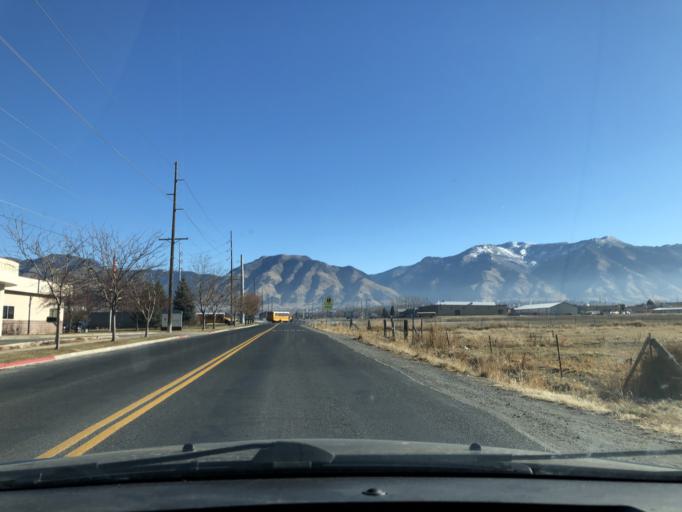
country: US
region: Utah
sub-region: Cache County
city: Logan
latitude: 41.7579
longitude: -111.8562
